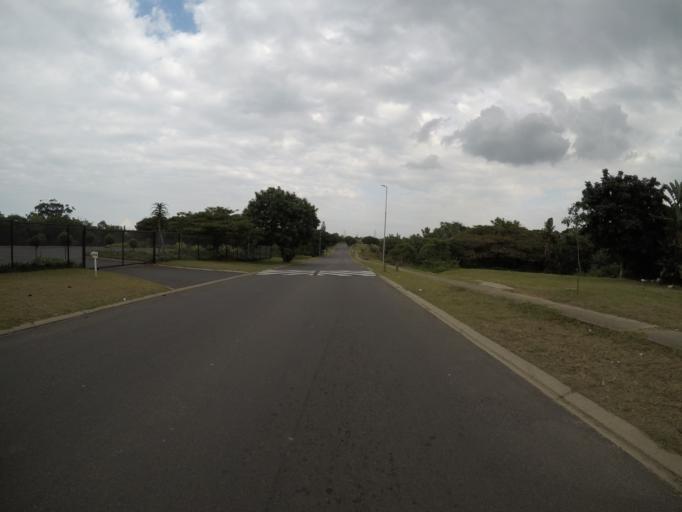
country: ZA
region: KwaZulu-Natal
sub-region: uThungulu District Municipality
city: Richards Bay
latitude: -28.7323
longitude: 32.0506
